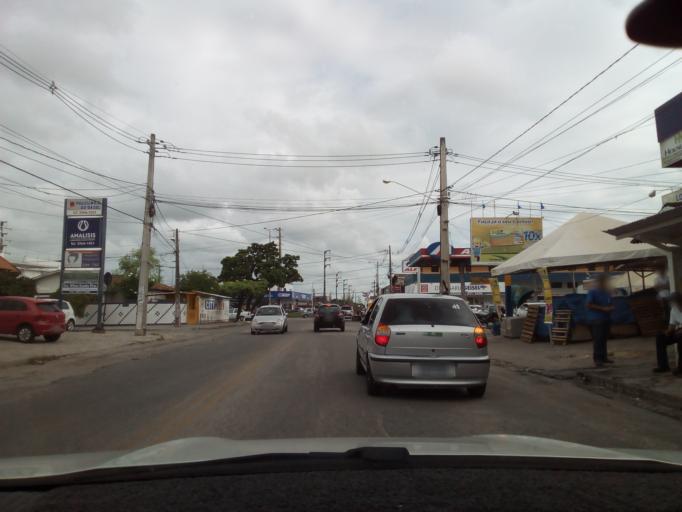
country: BR
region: Paraiba
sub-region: Joao Pessoa
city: Joao Pessoa
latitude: -7.1784
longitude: -34.8737
